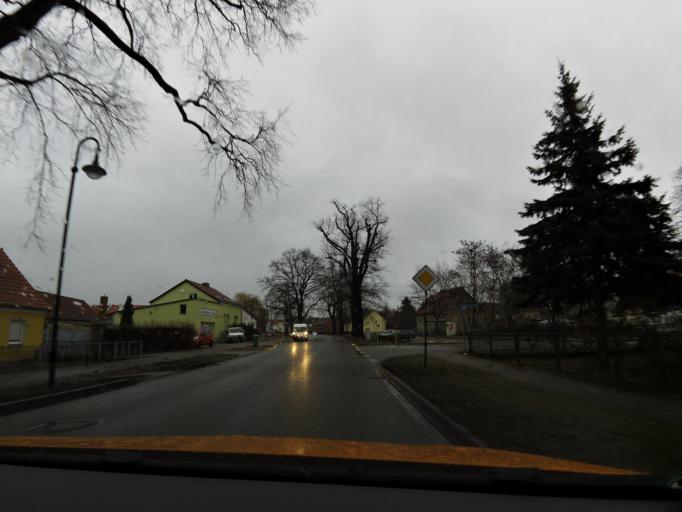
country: DE
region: Brandenburg
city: Rangsdorf
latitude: 52.2692
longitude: 13.4618
